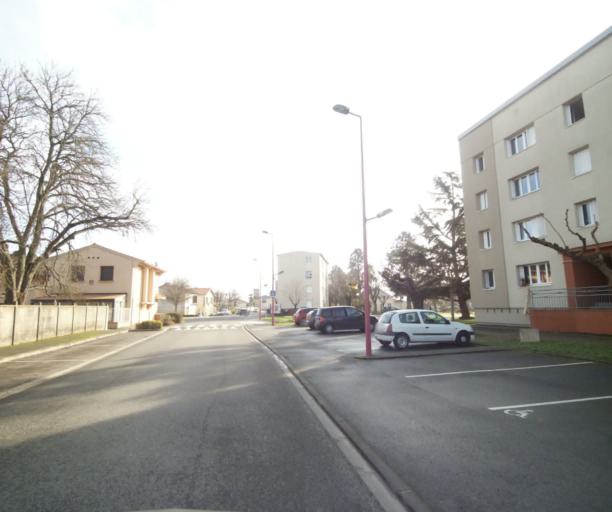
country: FR
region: Midi-Pyrenees
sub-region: Departement de la Haute-Garonne
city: Villemur-sur-Tarn
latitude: 43.8628
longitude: 1.4993
